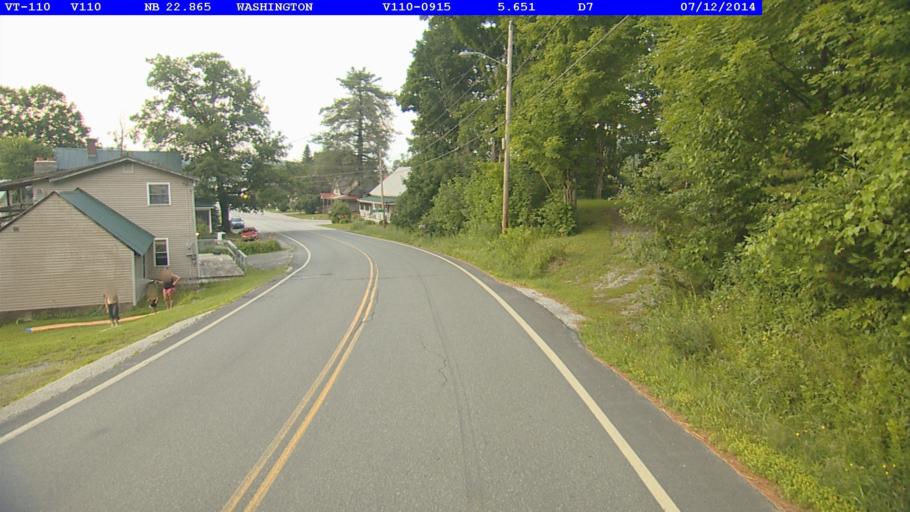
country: US
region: Vermont
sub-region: Washington County
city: South Barre
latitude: 44.1050
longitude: -72.4327
